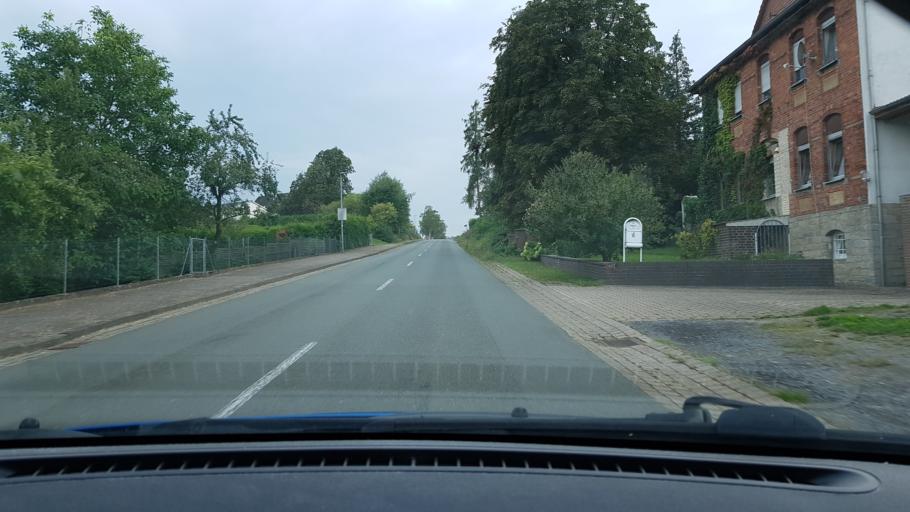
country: DE
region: Lower Saxony
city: Messenkamp
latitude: 52.2311
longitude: 9.3860
